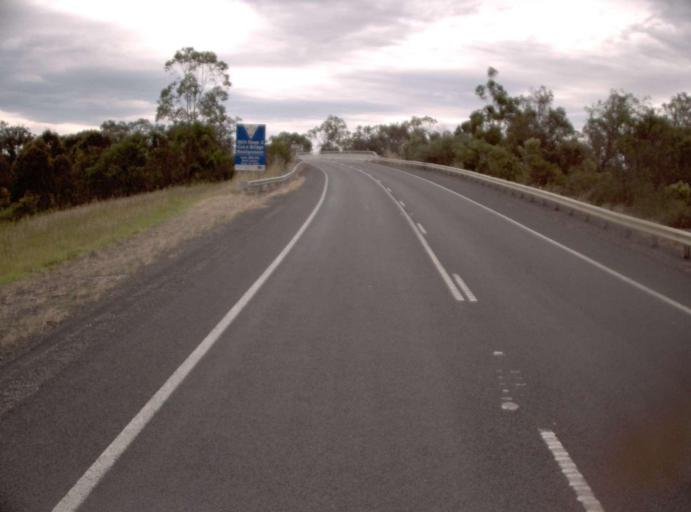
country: AU
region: Victoria
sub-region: Wellington
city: Sale
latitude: -38.1449
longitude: 147.0815
